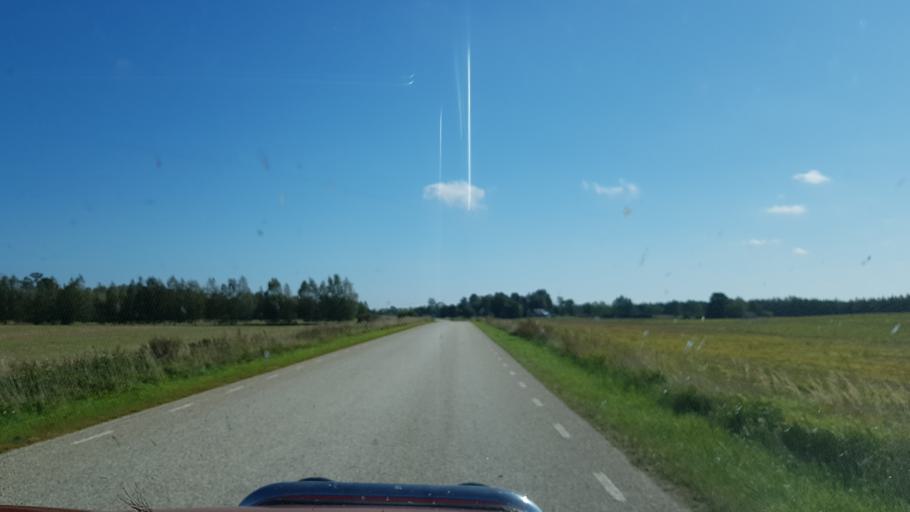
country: EE
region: Polvamaa
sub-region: Raepina vald
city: Rapina
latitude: 58.2316
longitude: 27.3560
